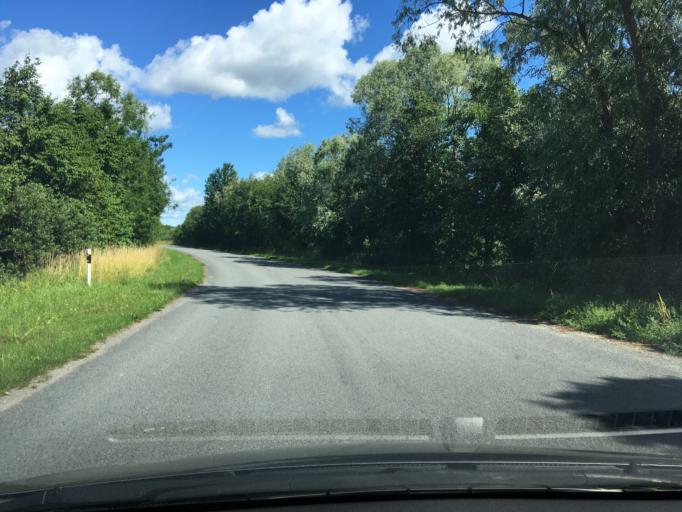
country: EE
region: Laeaene
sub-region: Lihula vald
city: Lihula
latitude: 58.7333
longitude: 23.9949
